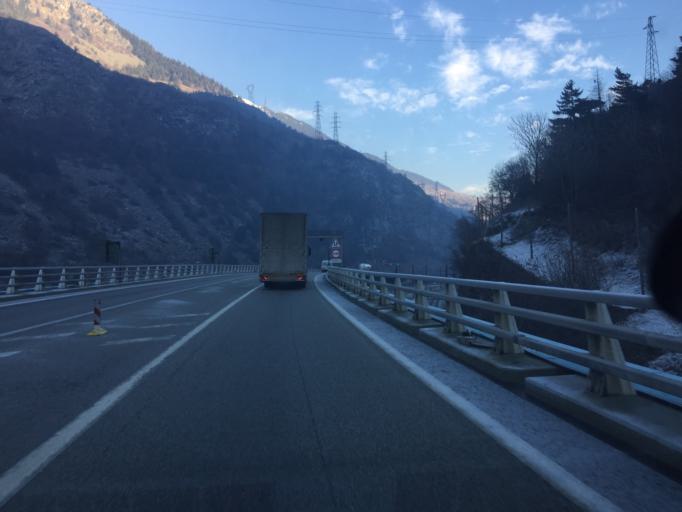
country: FR
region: Rhone-Alpes
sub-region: Departement de la Savoie
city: Saint-Michel-de-Maurienne
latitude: 45.2067
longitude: 6.5636
